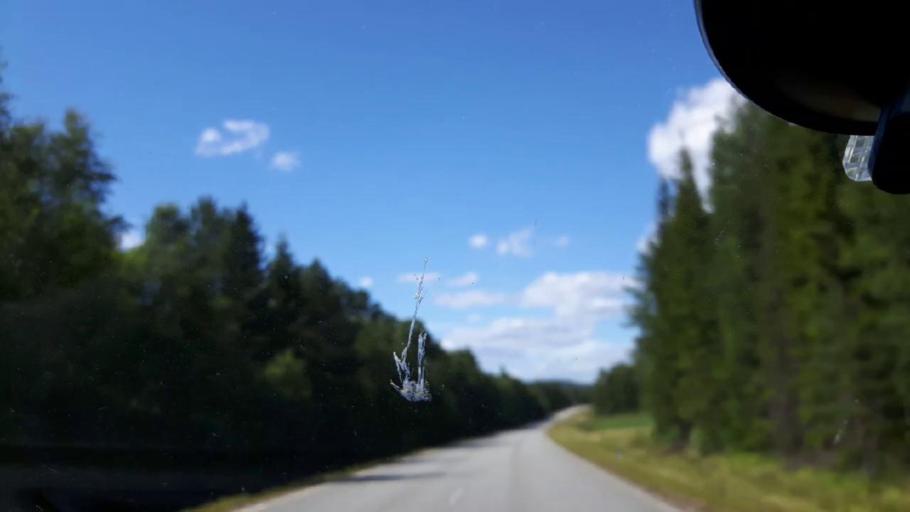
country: SE
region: Vaesternorrland
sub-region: Ange Kommun
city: Fransta
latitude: 62.7105
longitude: 16.3448
